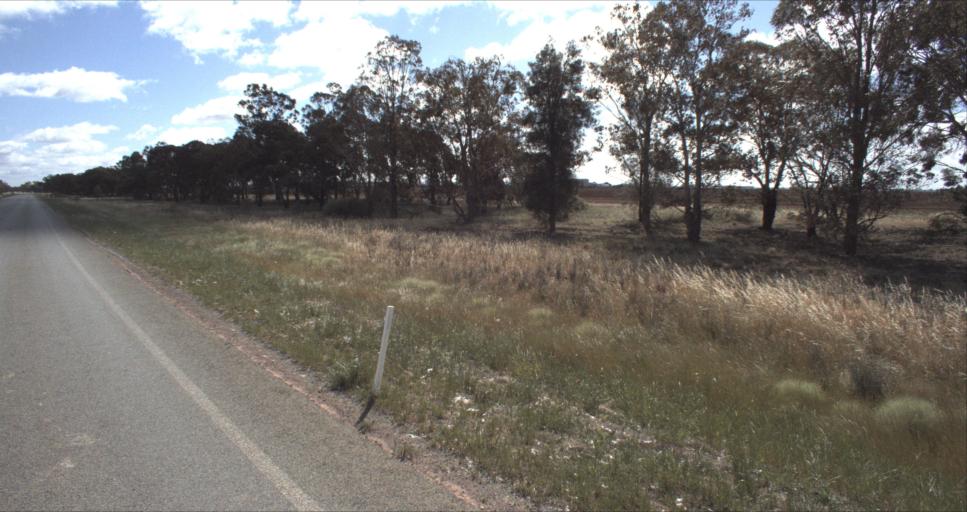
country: AU
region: New South Wales
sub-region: Murrumbidgee Shire
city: Darlington Point
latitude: -34.5800
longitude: 146.1652
